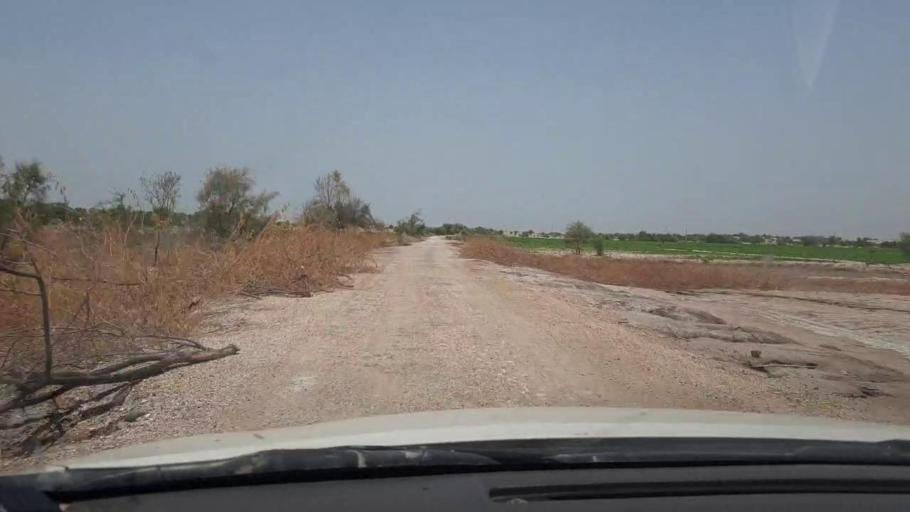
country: PK
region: Sindh
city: Rohri
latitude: 27.5105
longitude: 69.1845
